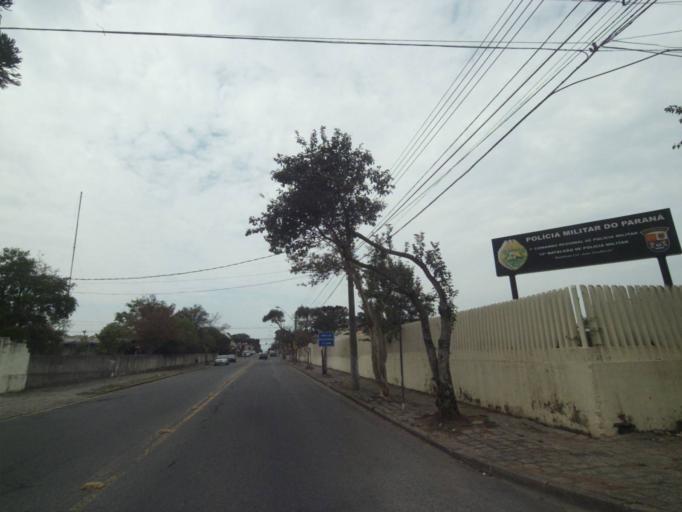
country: BR
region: Parana
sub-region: Curitiba
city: Curitiba
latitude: -25.4590
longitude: -49.3066
